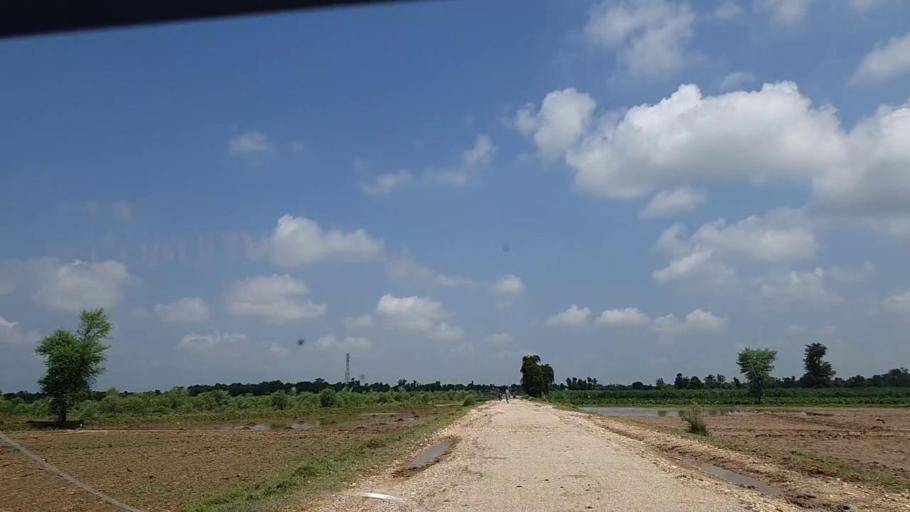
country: PK
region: Sindh
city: Tharu Shah
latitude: 26.9042
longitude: 68.0382
